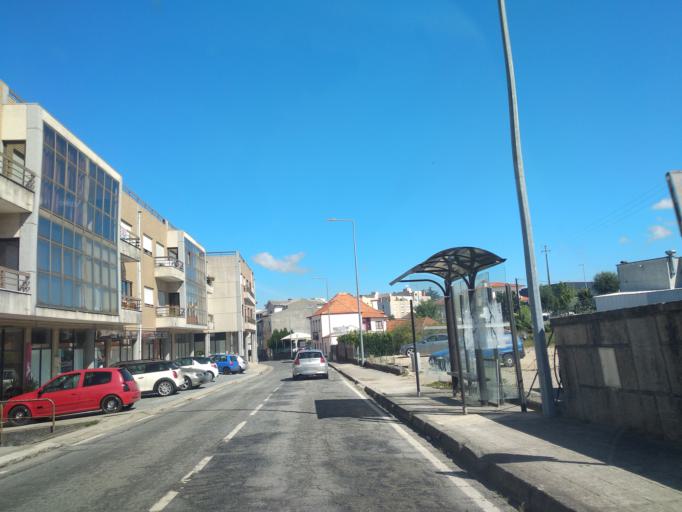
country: PT
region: Porto
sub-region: Pacos de Ferreira
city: Freamunde
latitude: 41.2859
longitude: -8.3338
